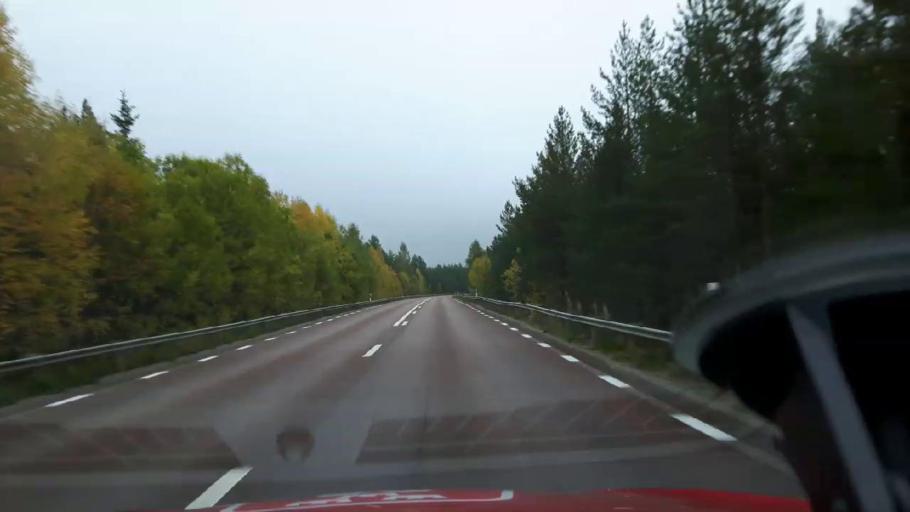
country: SE
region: Jaemtland
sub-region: Bergs Kommun
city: Hoverberg
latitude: 62.6156
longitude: 14.3868
